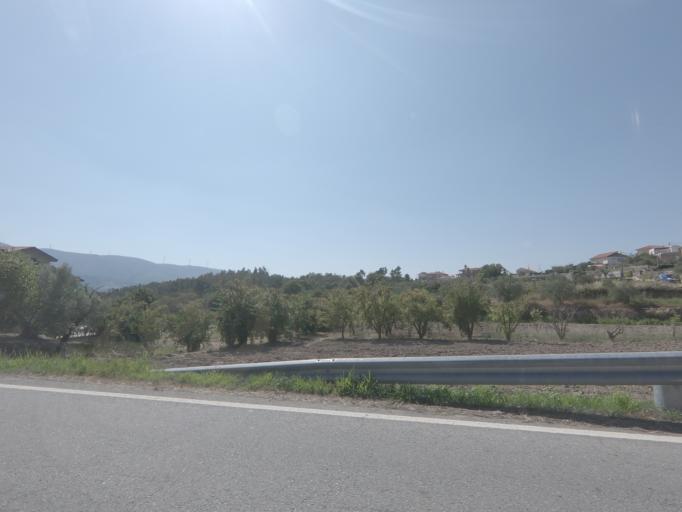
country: PT
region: Viseu
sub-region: Tarouca
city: Tarouca
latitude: 41.0290
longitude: -7.7450
